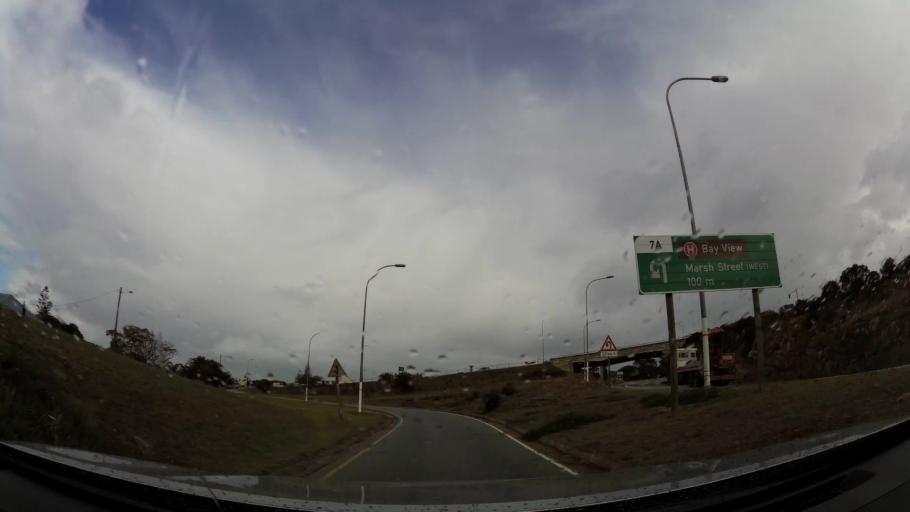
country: ZA
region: Western Cape
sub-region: Eden District Municipality
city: Mossel Bay
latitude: -34.1814
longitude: 22.1342
